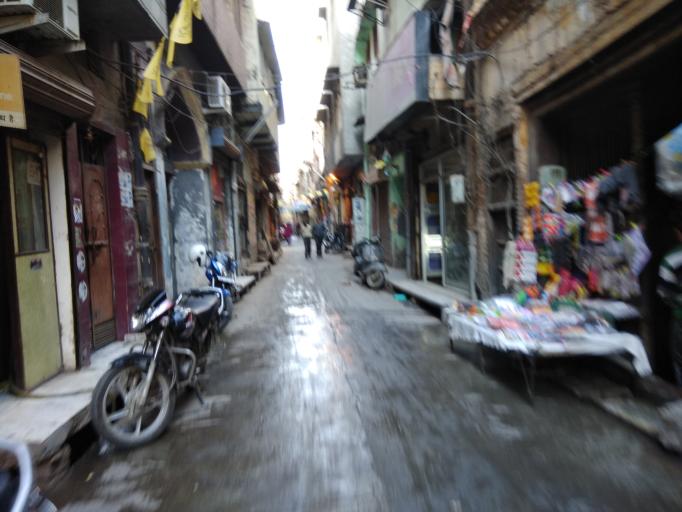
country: IN
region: Punjab
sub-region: Amritsar
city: Amritsar
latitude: 31.6170
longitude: 74.8755
